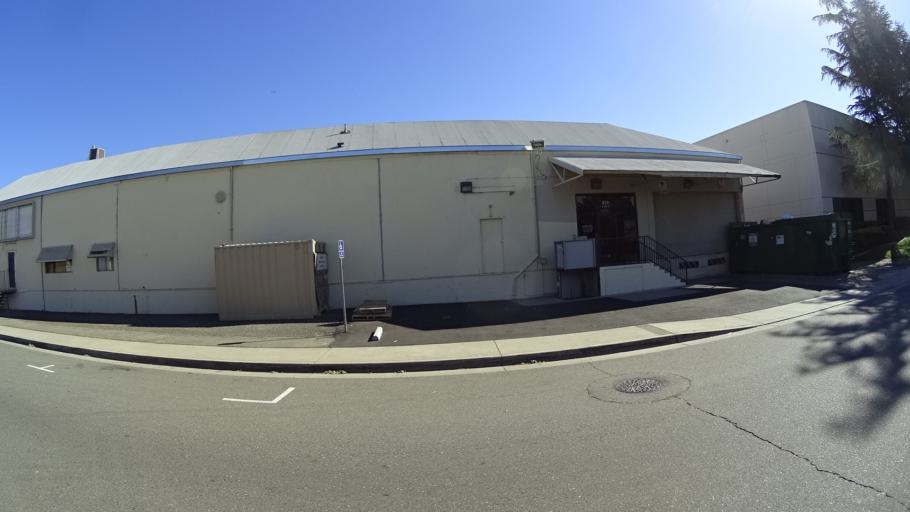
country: US
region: California
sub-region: Sacramento County
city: Sacramento
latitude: 38.5982
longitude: -121.4846
